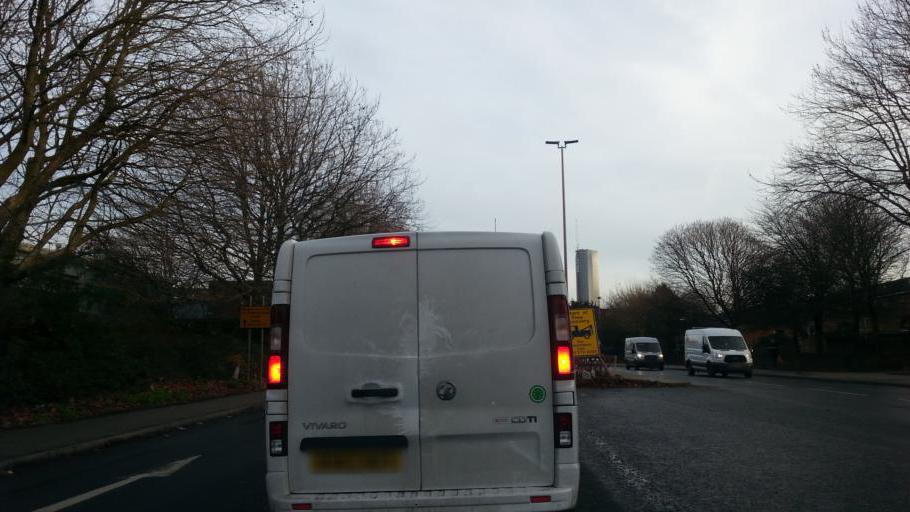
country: GB
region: England
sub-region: City and Borough of Salford
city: Salford
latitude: 53.4770
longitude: -2.2714
